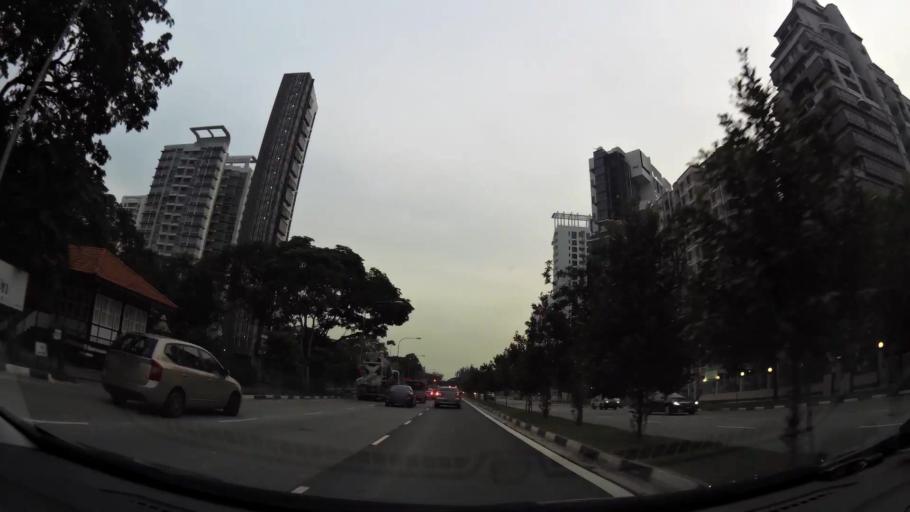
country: SG
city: Singapore
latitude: 1.2999
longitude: 103.8855
